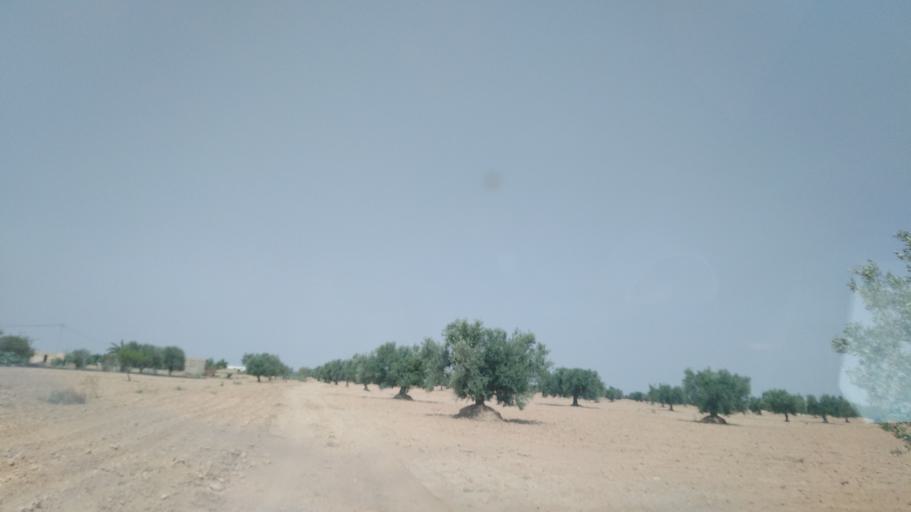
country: TN
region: Safaqis
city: Sfax
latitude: 34.6543
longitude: 10.5561
